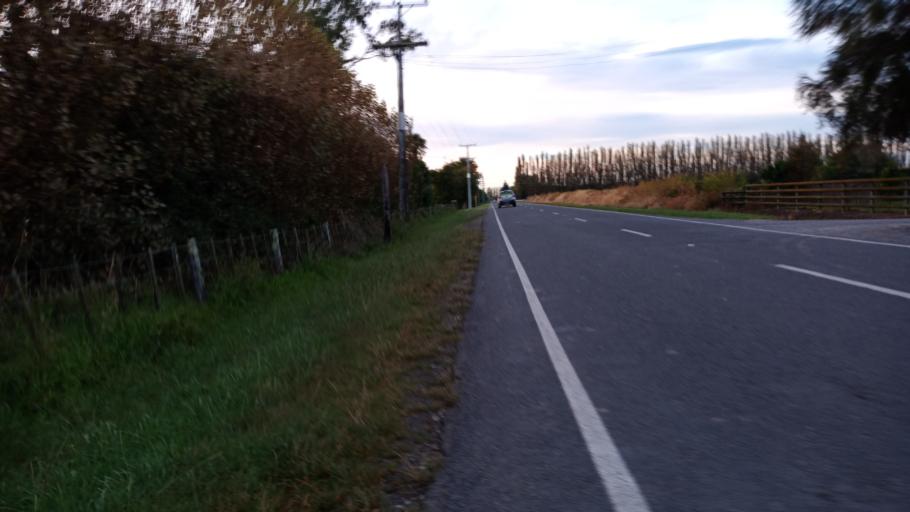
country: NZ
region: Gisborne
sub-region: Gisborne District
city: Gisborne
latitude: -38.6465
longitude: 177.9444
